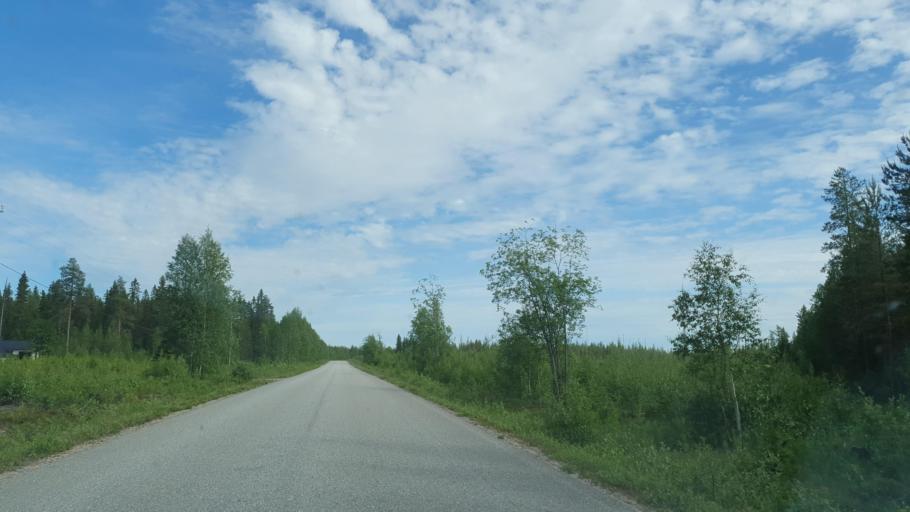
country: FI
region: Kainuu
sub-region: Kehys-Kainuu
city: Suomussalmi
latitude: 64.5500
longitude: 29.2323
